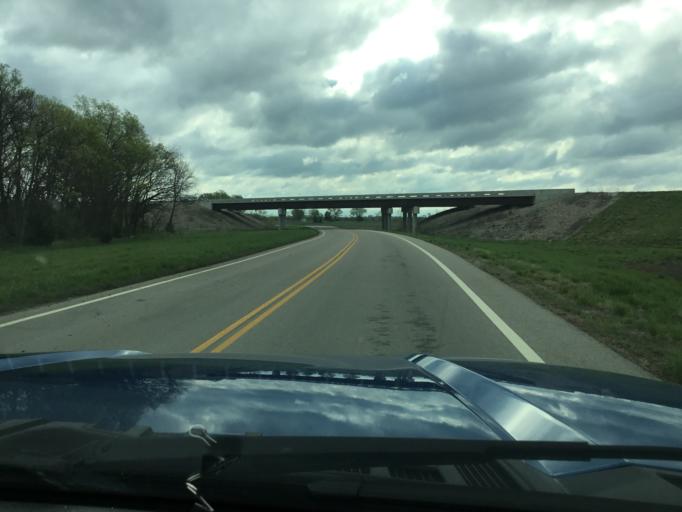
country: US
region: Kansas
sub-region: Douglas County
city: Lawrence
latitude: 38.9278
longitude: -95.1830
